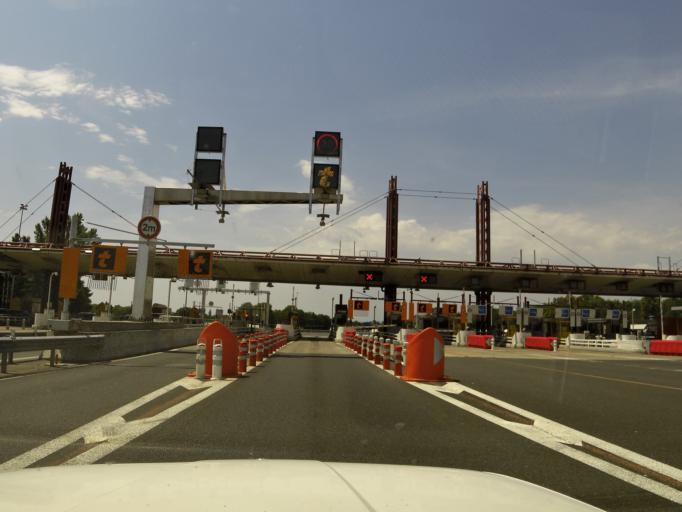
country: FR
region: Rhone-Alpes
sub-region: Departement de l'Ain
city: Beynost
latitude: 45.8208
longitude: 4.9945
